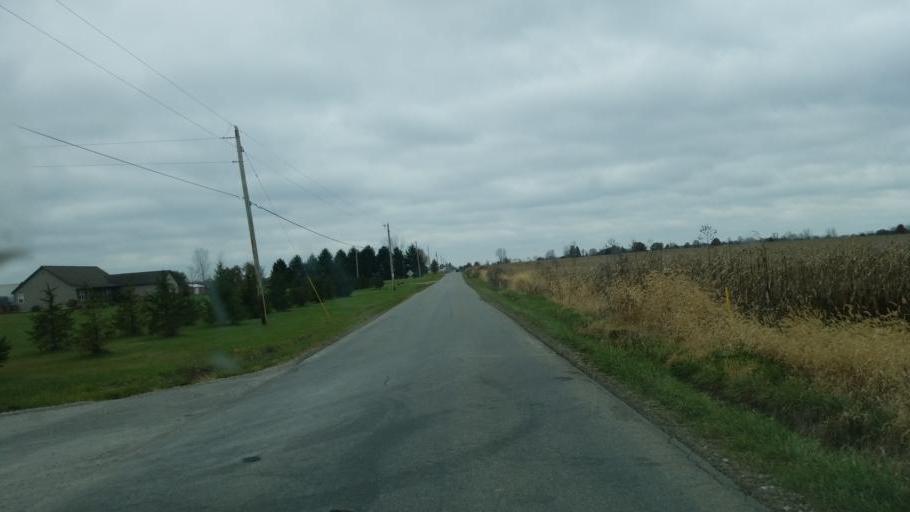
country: US
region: Ohio
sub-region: Licking County
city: Johnstown
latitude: 40.1716
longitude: -82.7584
